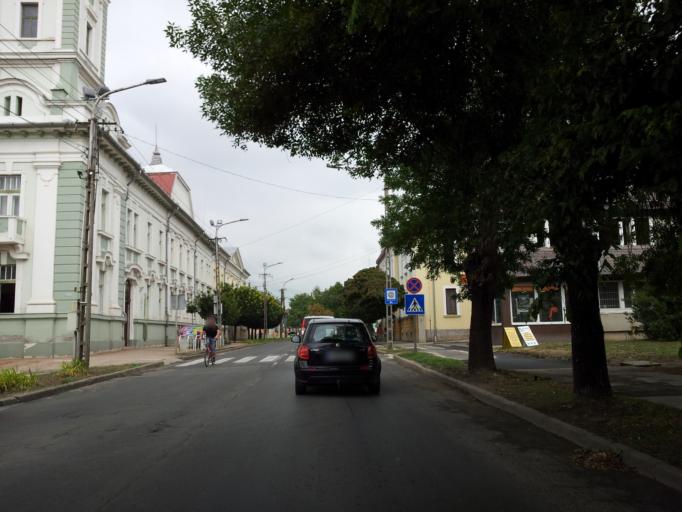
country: HU
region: Tolna
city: Tamasi
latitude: 46.6314
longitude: 18.2817
